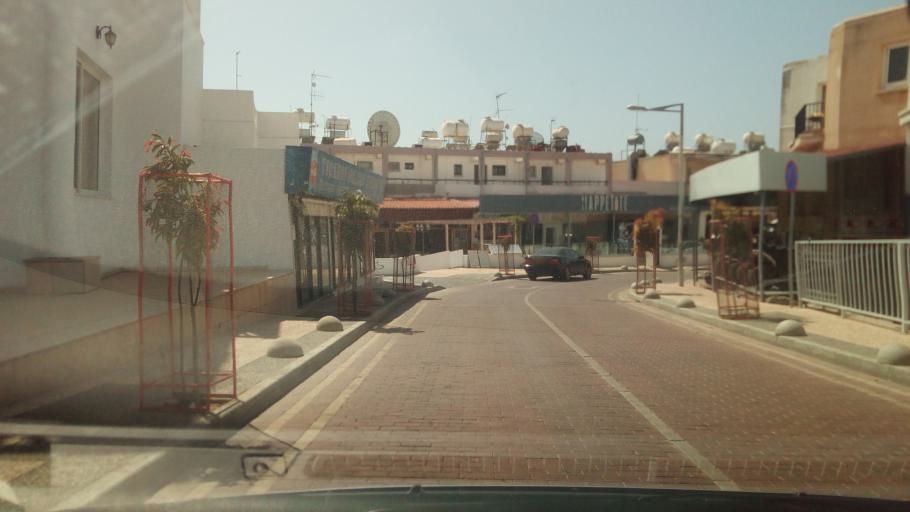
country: CY
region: Ammochostos
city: Ayia Napa
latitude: 34.9879
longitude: 33.9959
